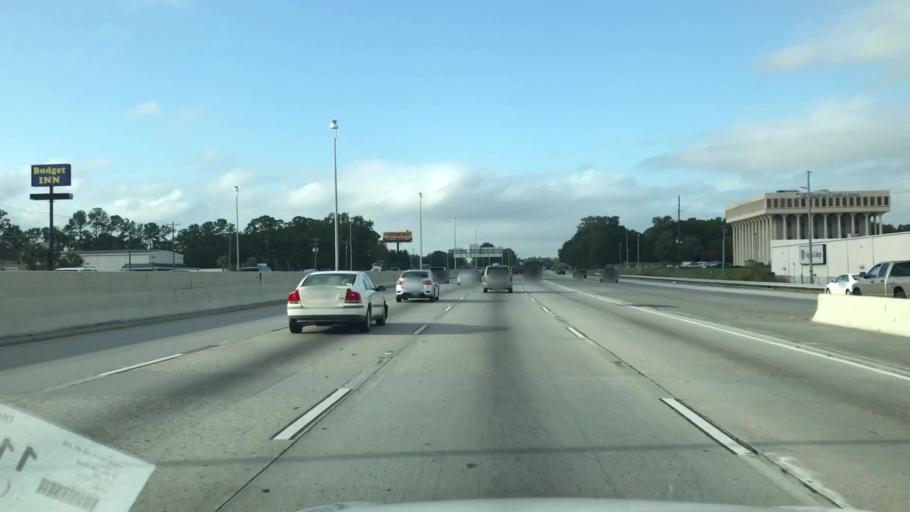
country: US
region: South Carolina
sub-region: Berkeley County
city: Hanahan
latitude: 32.9056
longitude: -80.0250
